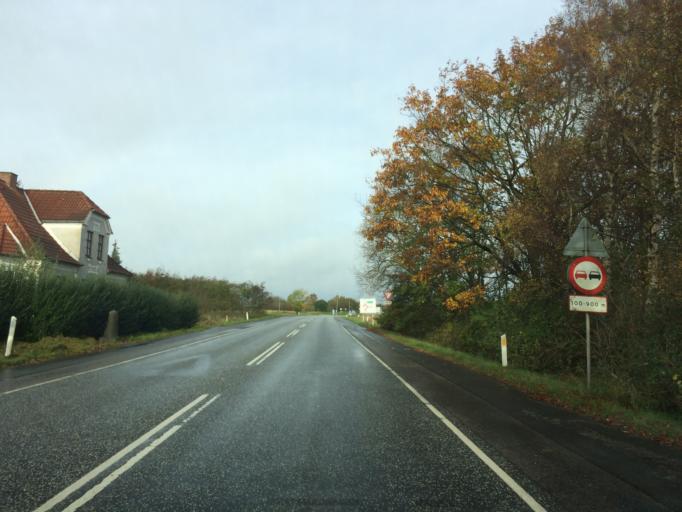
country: DK
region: South Denmark
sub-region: Fredericia Kommune
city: Taulov
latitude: 55.5328
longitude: 9.6383
